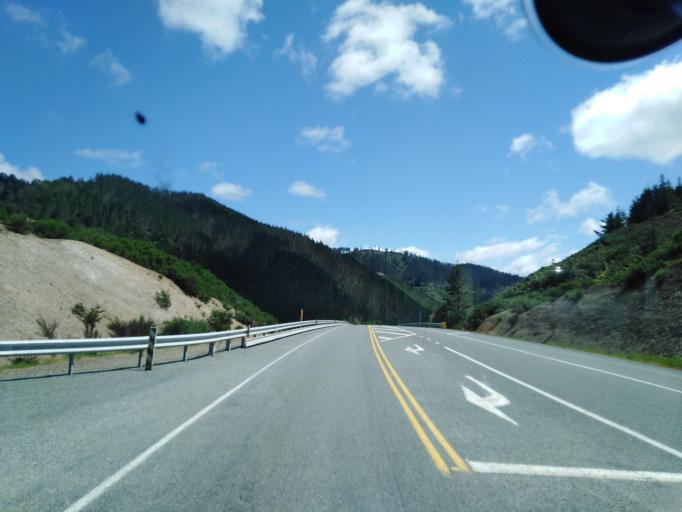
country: NZ
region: Nelson
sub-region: Nelson City
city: Nelson
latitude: -41.1906
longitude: 173.5541
